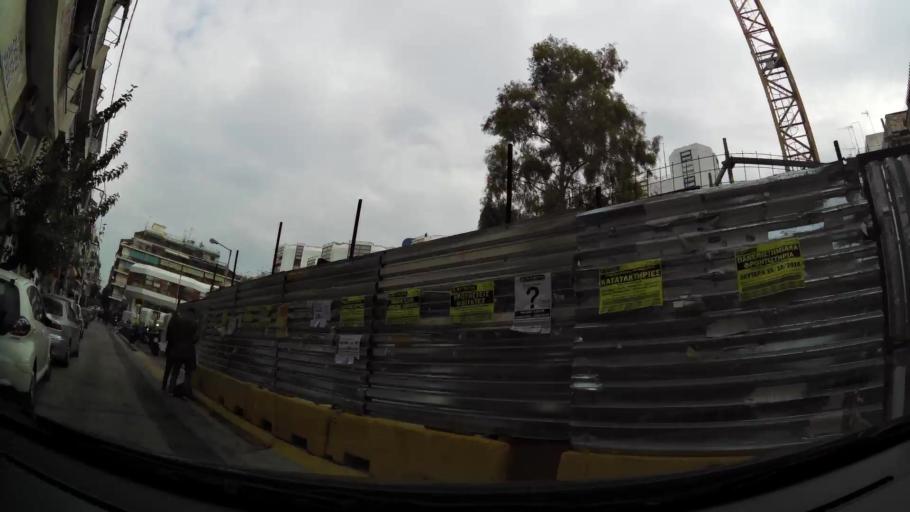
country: GR
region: Attica
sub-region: Nomos Attikis
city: Piraeus
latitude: 37.9415
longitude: 23.6522
